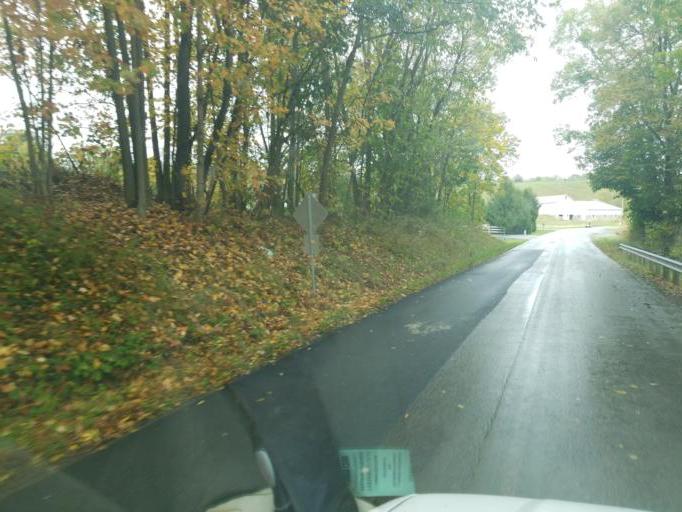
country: US
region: Ohio
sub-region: Wayne County
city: Shreve
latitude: 40.5908
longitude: -82.0151
